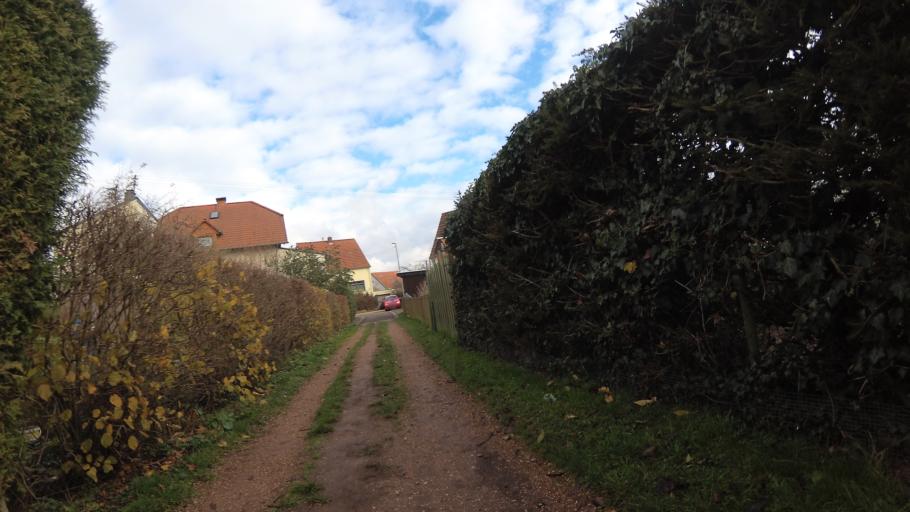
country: DE
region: Saarland
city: Oberthal
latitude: 49.5115
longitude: 7.0870
